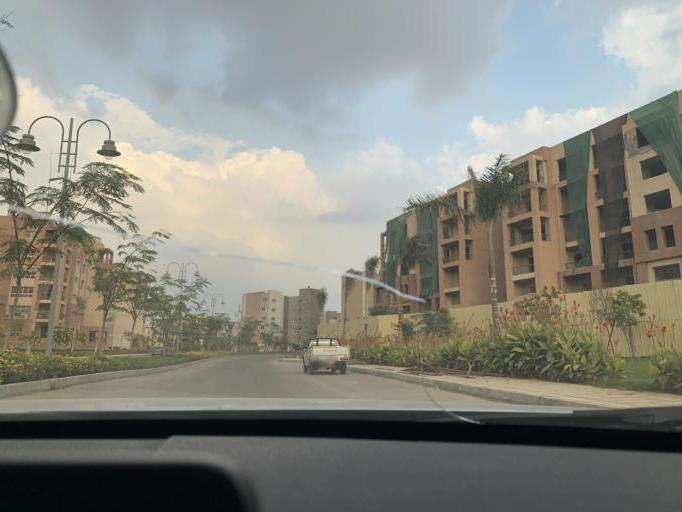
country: EG
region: Muhafazat al Qalyubiyah
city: Al Khankah
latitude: 30.1023
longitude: 31.6490
